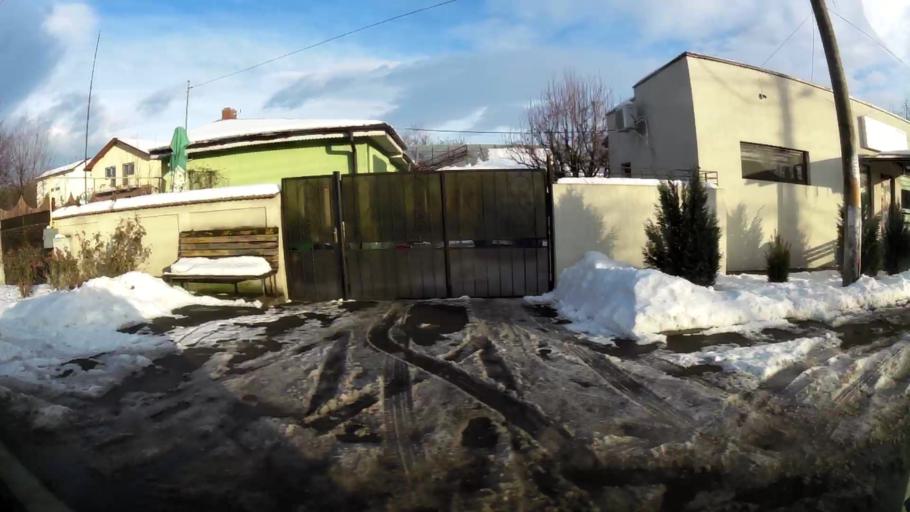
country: RO
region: Ilfov
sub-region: Comuna Jilava
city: Jilava
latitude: 44.3399
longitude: 26.0837
